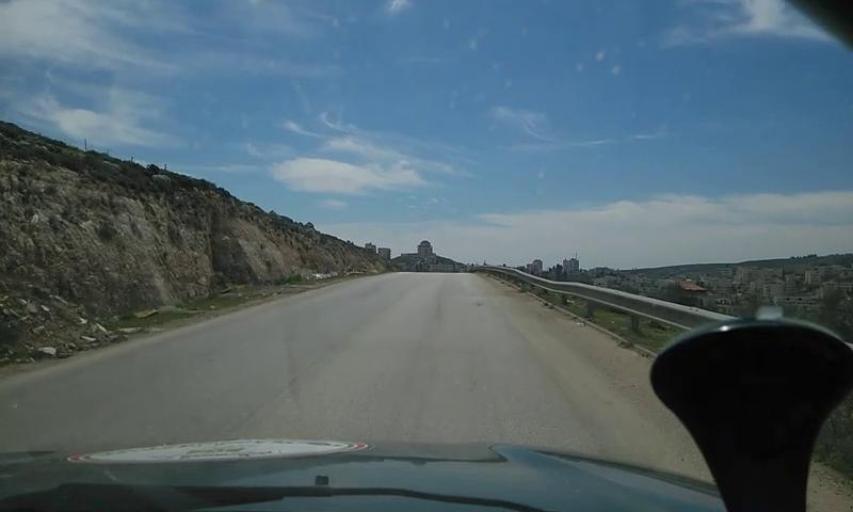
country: PS
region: West Bank
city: Al Judayrah
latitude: 31.8570
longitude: 35.2014
